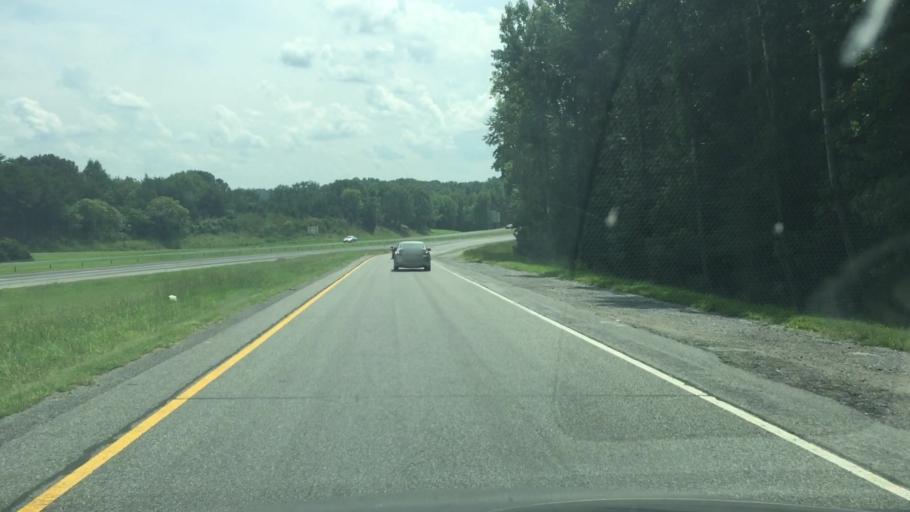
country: US
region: North Carolina
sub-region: Rockingham County
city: Reidsville
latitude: 36.3591
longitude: -79.6289
